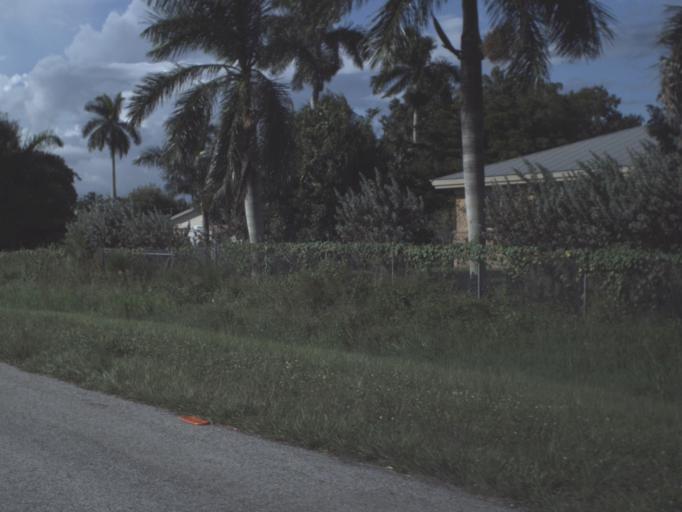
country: US
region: Florida
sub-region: Charlotte County
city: Punta Gorda
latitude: 26.9407
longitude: -82.0295
